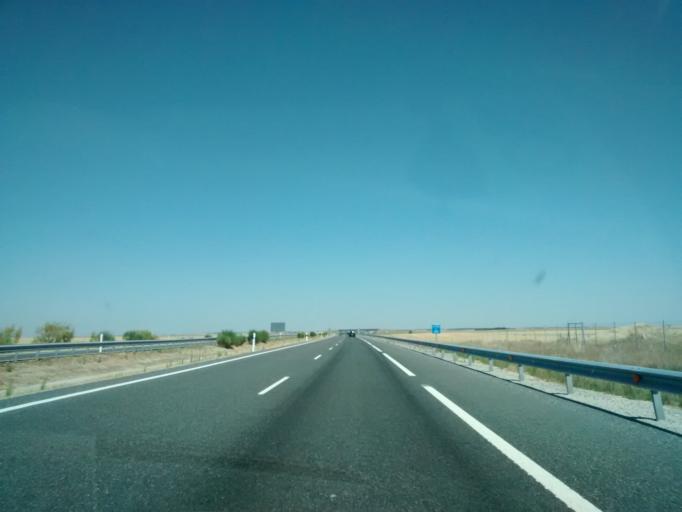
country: ES
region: Castille and Leon
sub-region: Provincia de Avila
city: Narros del Castillo
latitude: 40.8821
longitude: -5.0420
